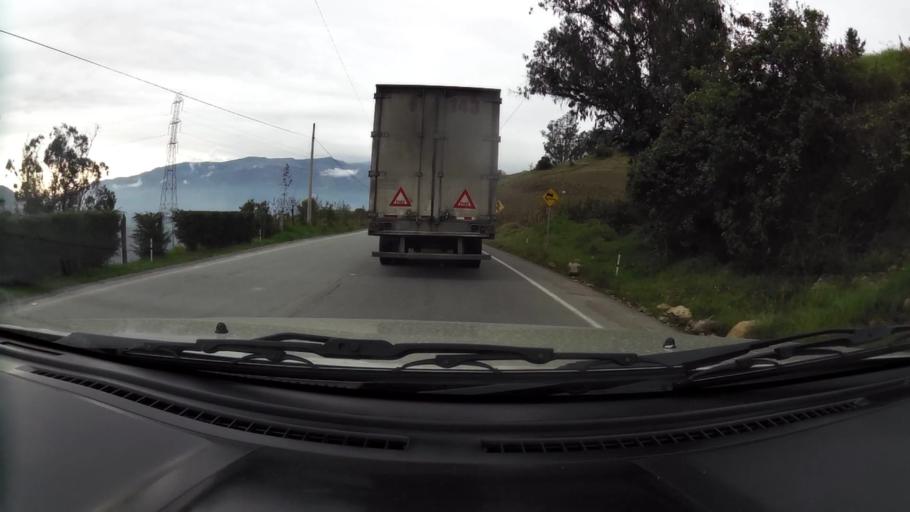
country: EC
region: Chimborazo
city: Alausi
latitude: -2.3084
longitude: -78.9280
